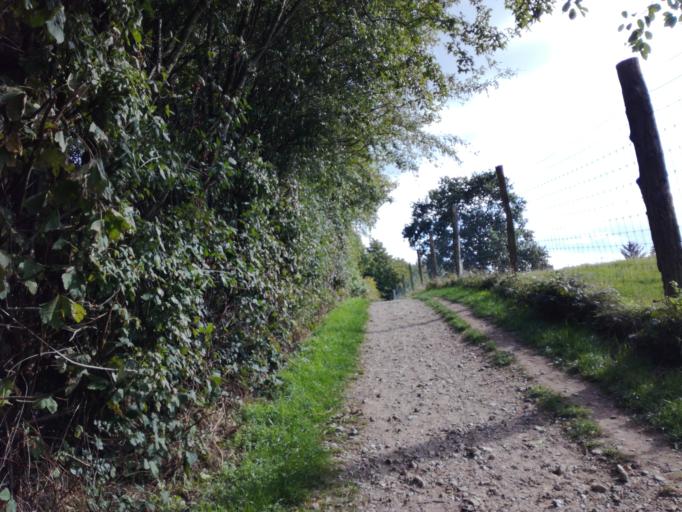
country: DK
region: South Denmark
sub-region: Fredericia Kommune
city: Snoghoj
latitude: 55.5130
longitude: 9.7078
